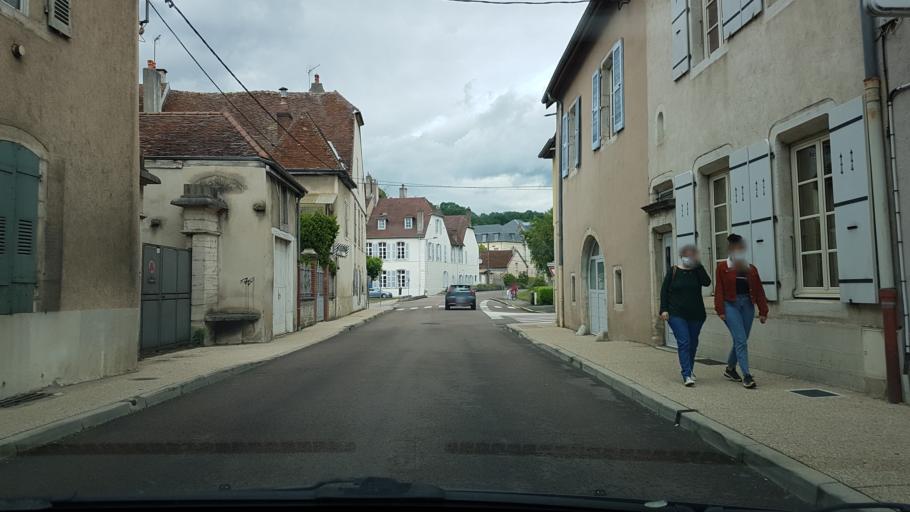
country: FR
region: Franche-Comte
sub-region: Departement du Jura
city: Lons-le-Saunier
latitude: 46.6771
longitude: 5.5552
